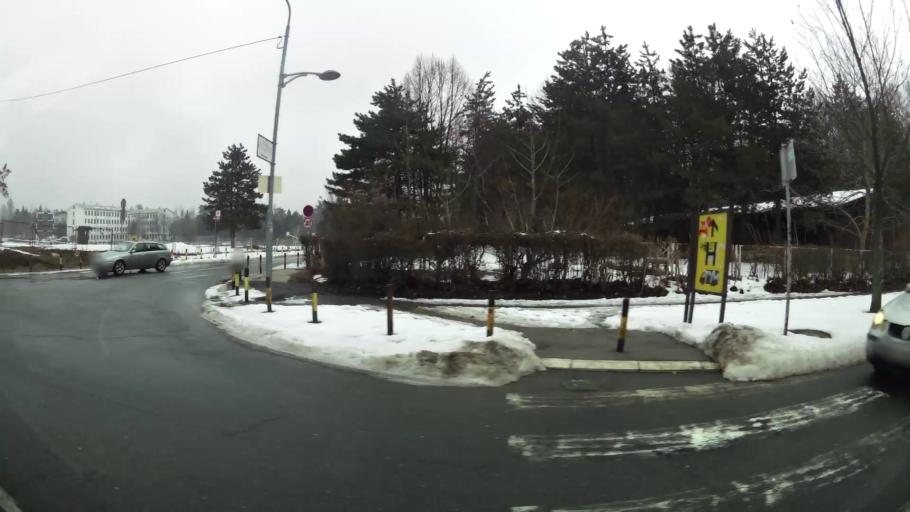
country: RS
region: Central Serbia
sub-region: Belgrade
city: Savski Venac
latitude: 44.7659
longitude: 20.4634
